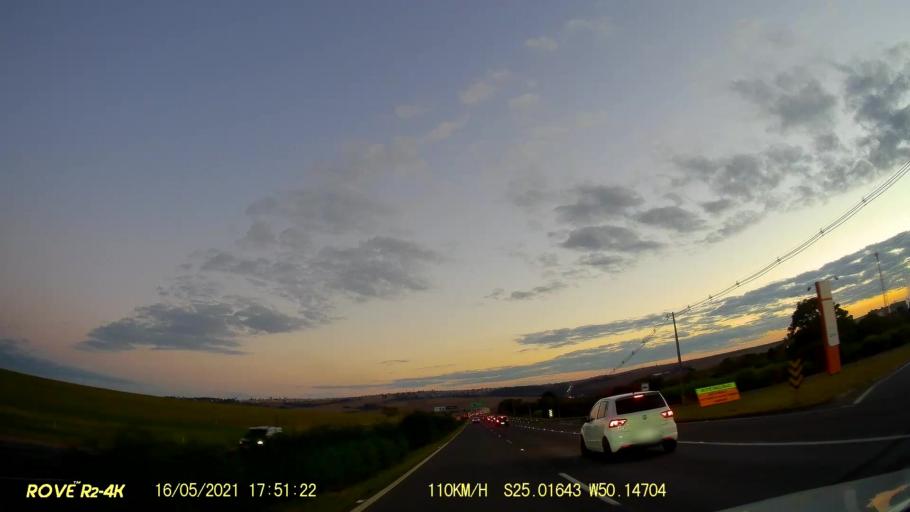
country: BR
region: Parana
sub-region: Carambei
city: Carambei
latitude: -25.0165
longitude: -50.1470
